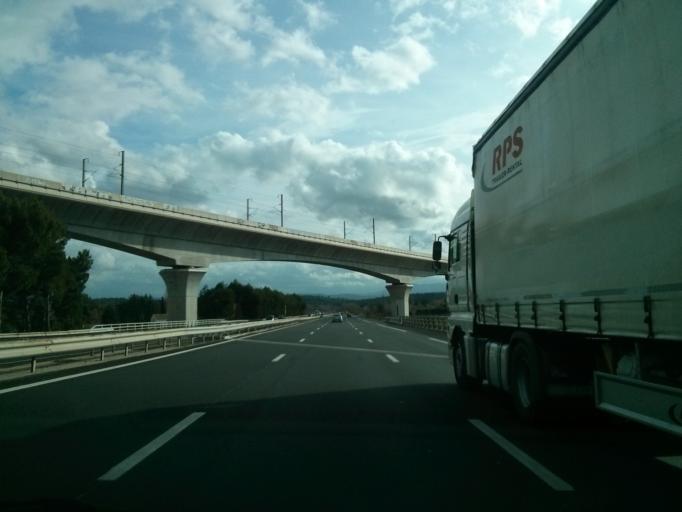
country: FR
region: Provence-Alpes-Cote d'Azur
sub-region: Departement des Bouches-du-Rhone
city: Eguilles
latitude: 43.5467
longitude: 5.3294
